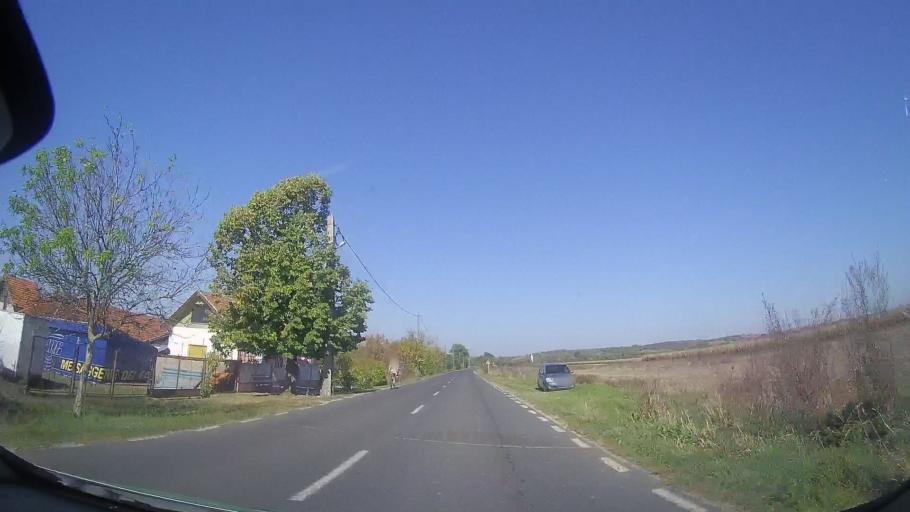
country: RO
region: Timis
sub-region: Comuna Balint
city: Balint
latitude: 45.8034
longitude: 21.8620
